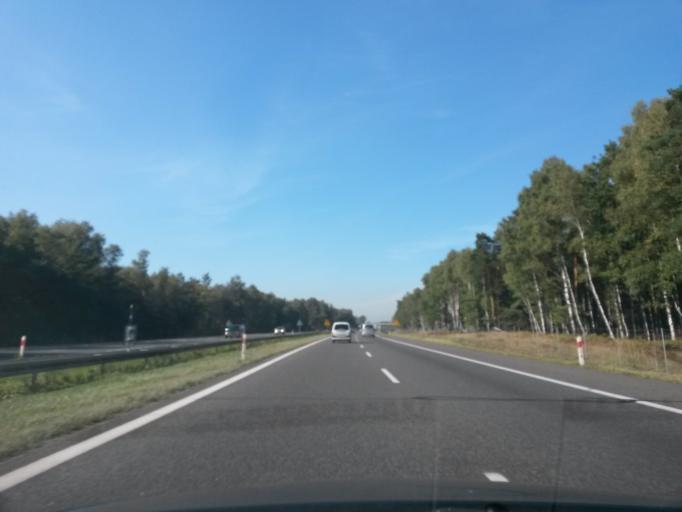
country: PL
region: Lesser Poland Voivodeship
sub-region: Powiat chrzanowski
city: Regulice
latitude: 50.1065
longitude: 19.5212
